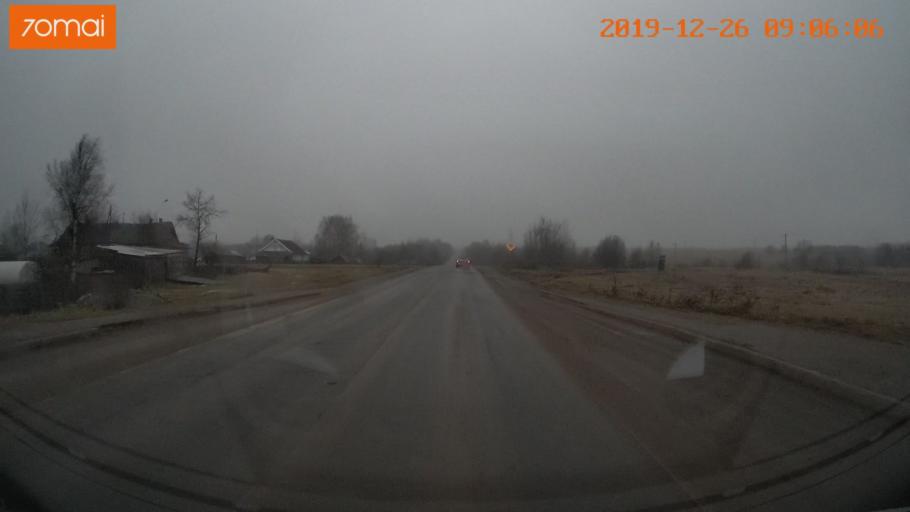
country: RU
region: Vologda
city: Gryazovets
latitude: 58.8325
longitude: 40.2549
